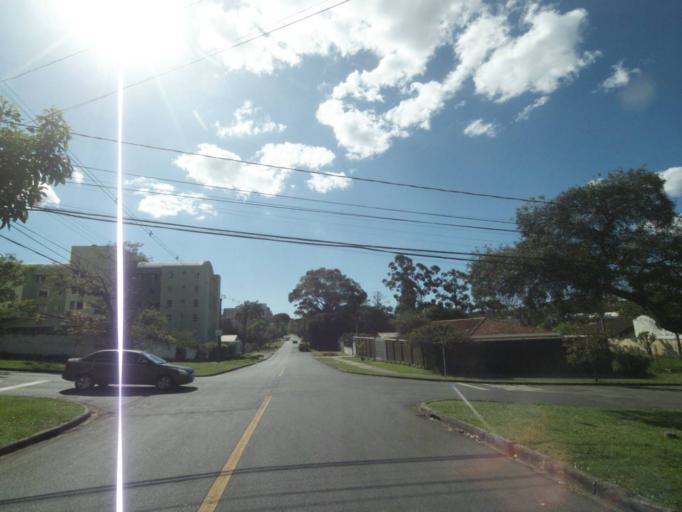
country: BR
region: Parana
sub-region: Curitiba
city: Curitiba
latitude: -25.3892
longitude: -49.2406
